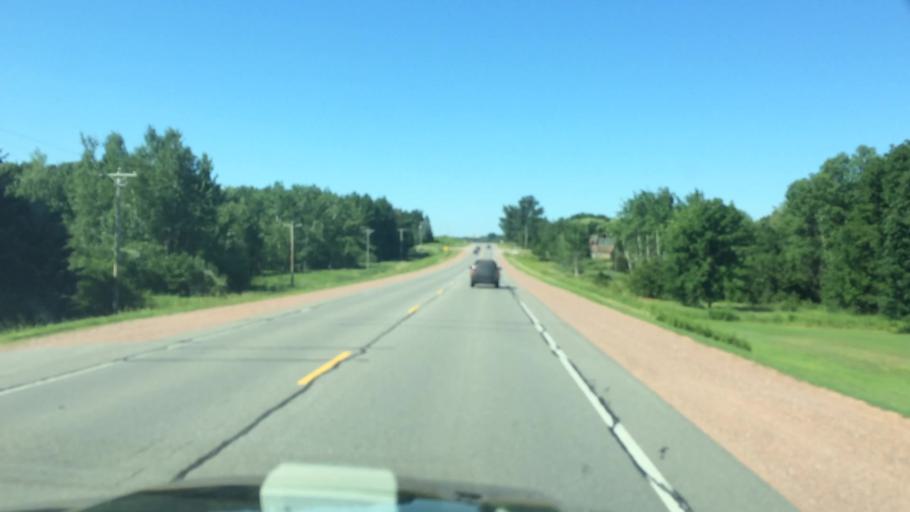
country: US
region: Wisconsin
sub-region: Wood County
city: Marshfield
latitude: 44.7128
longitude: -90.1162
